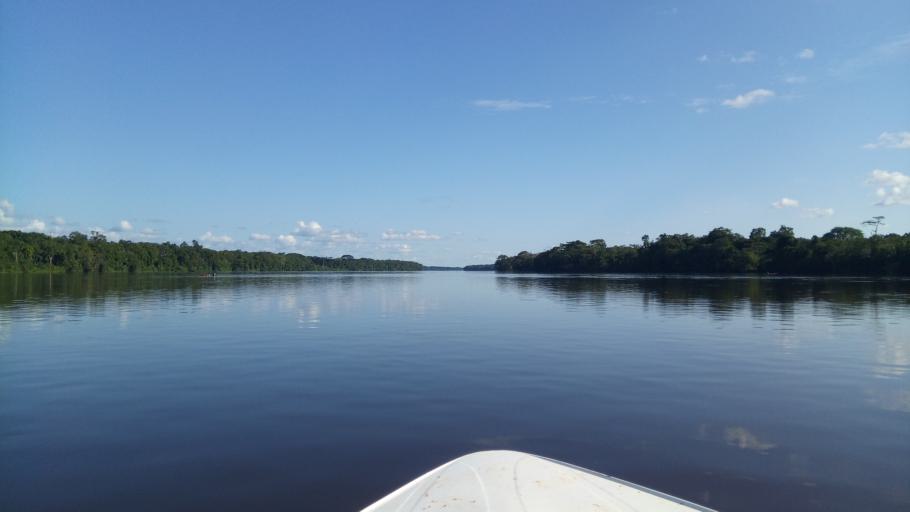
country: CD
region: Eastern Province
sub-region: Sous-Region de la Tshopo
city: Yangambi
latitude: 0.4427
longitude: 24.1628
